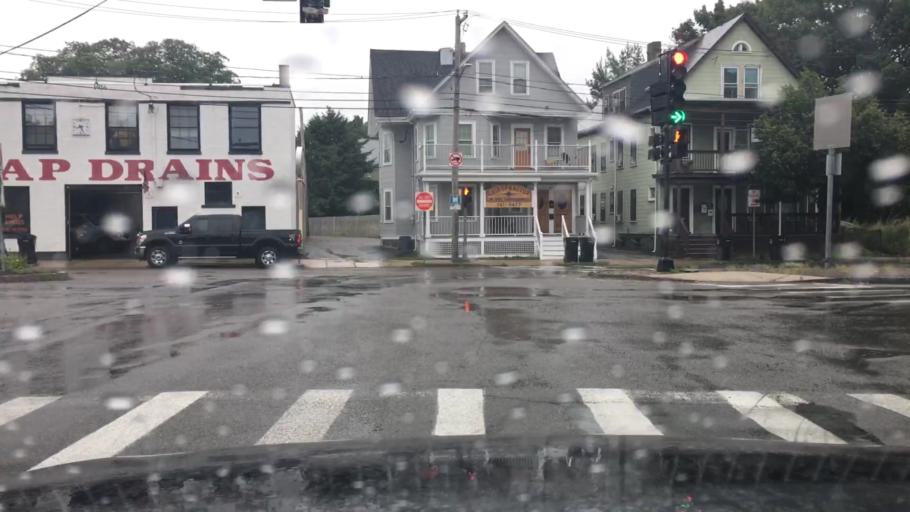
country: US
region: Massachusetts
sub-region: Essex County
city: Salem
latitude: 42.5180
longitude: -70.9058
